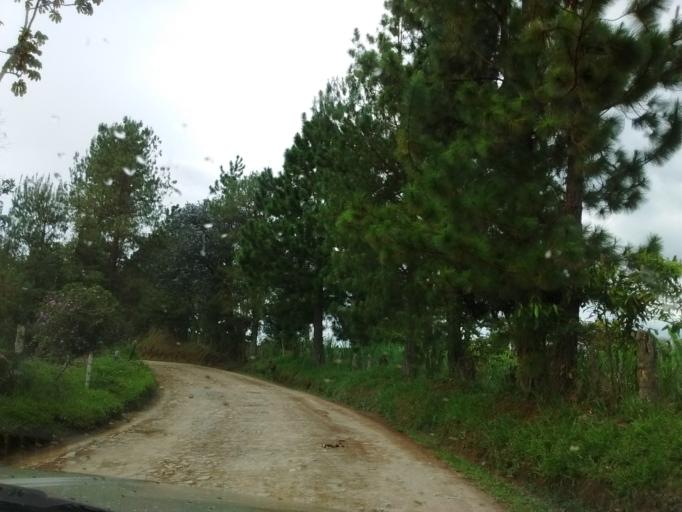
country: CO
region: Cauca
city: Cajibio
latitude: 2.5835
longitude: -76.6790
